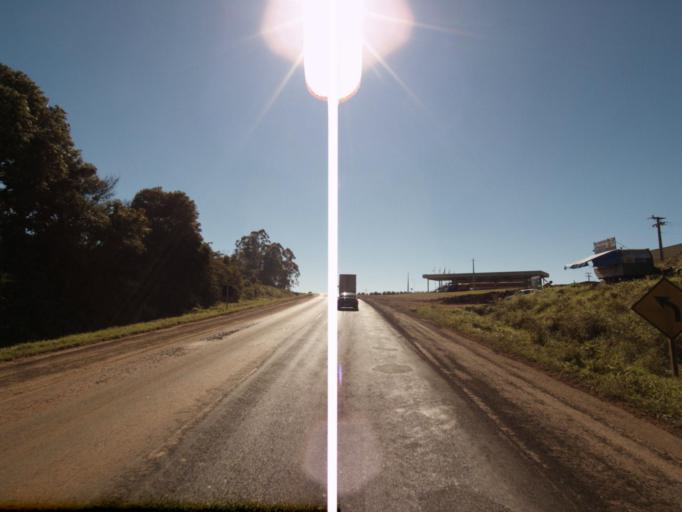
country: BR
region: Rio Grande do Sul
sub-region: Frederico Westphalen
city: Frederico Westphalen
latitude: -26.9079
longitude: -53.1873
